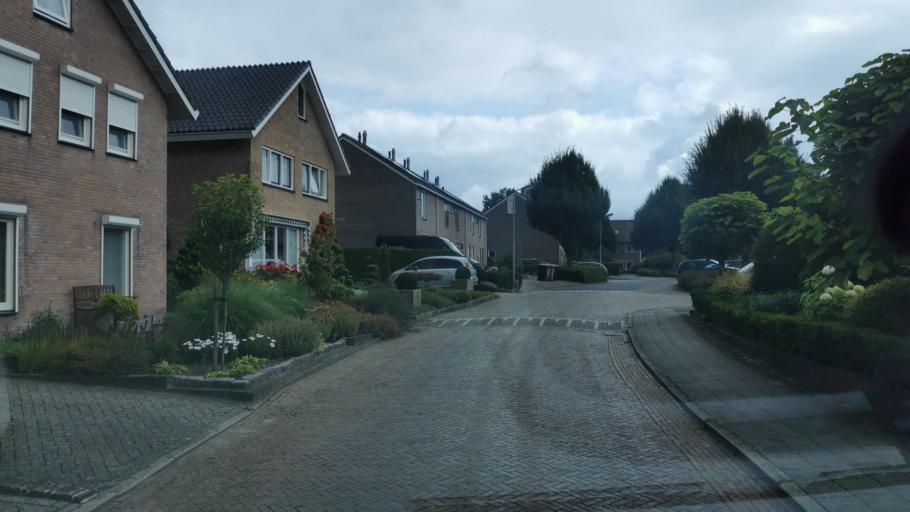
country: NL
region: Overijssel
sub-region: Gemeente Losser
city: Losser
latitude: 52.3116
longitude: 6.9921
